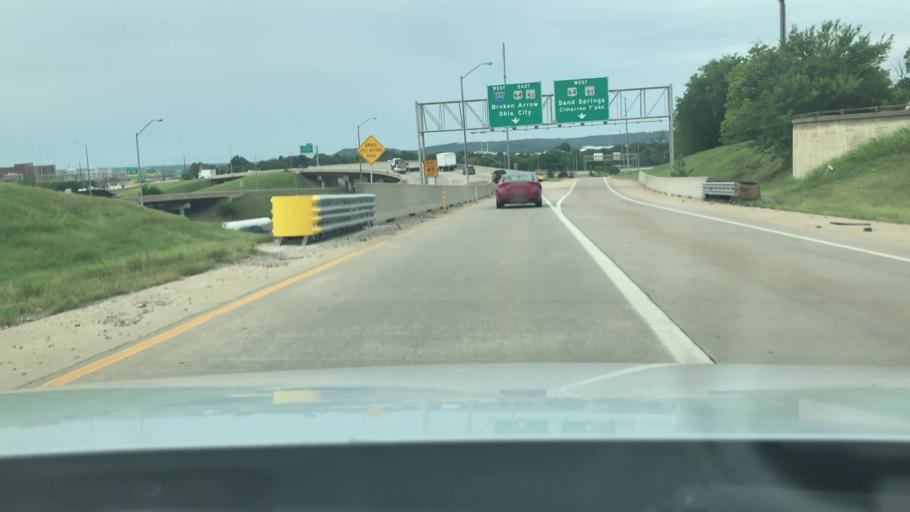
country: US
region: Oklahoma
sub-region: Tulsa County
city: Tulsa
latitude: 36.1608
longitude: -96.0013
